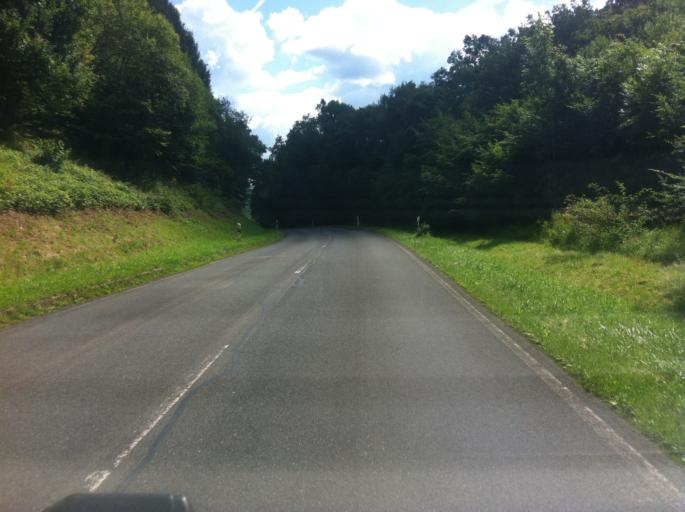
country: DE
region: Rheinland-Pfalz
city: Kalenborn-Scheuern
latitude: 50.2331
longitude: 6.6233
